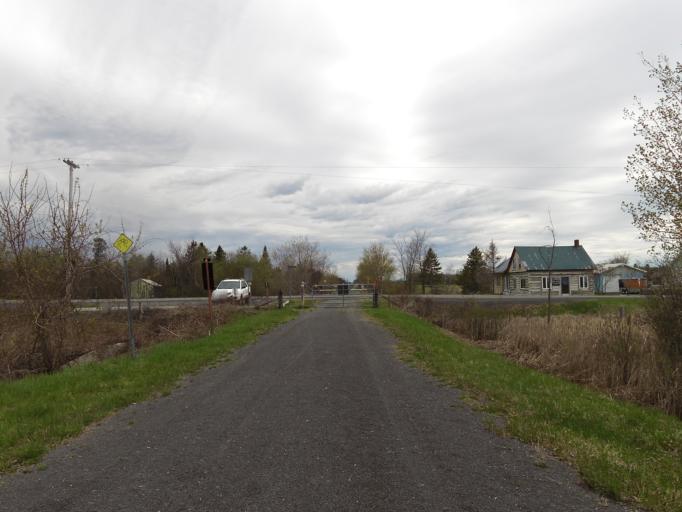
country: CA
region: Ontario
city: Hawkesbury
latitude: 45.5440
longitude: -74.8013
